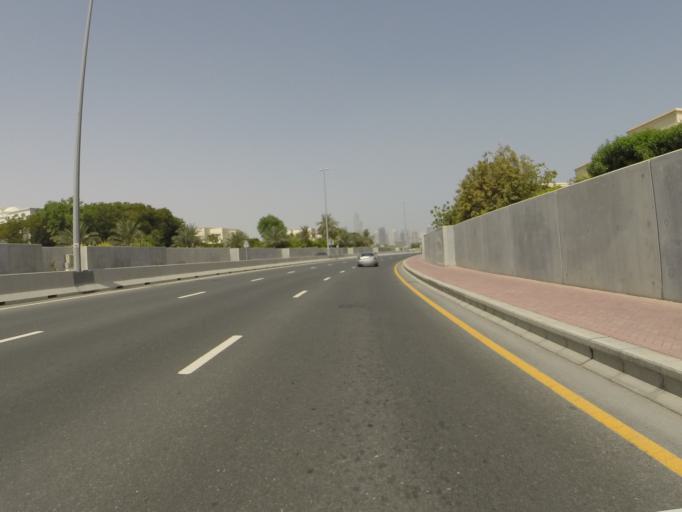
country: AE
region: Dubai
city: Dubai
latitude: 25.0762
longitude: 55.1747
